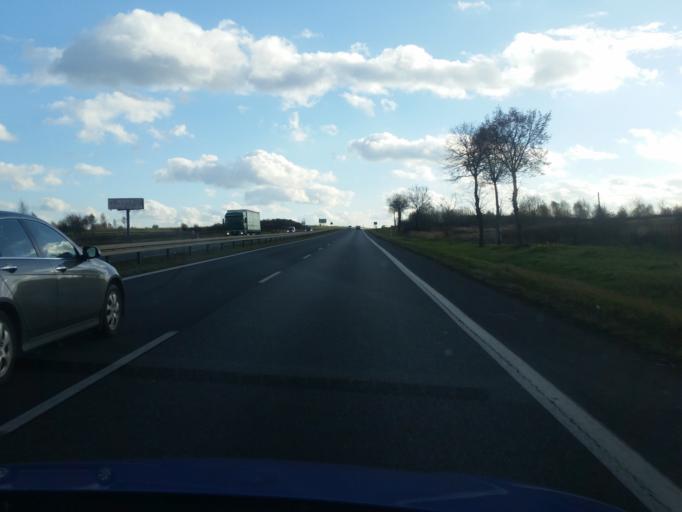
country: PL
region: Silesian Voivodeship
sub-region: Powiat myszkowski
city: Kozieglowy
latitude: 50.5862
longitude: 19.1628
